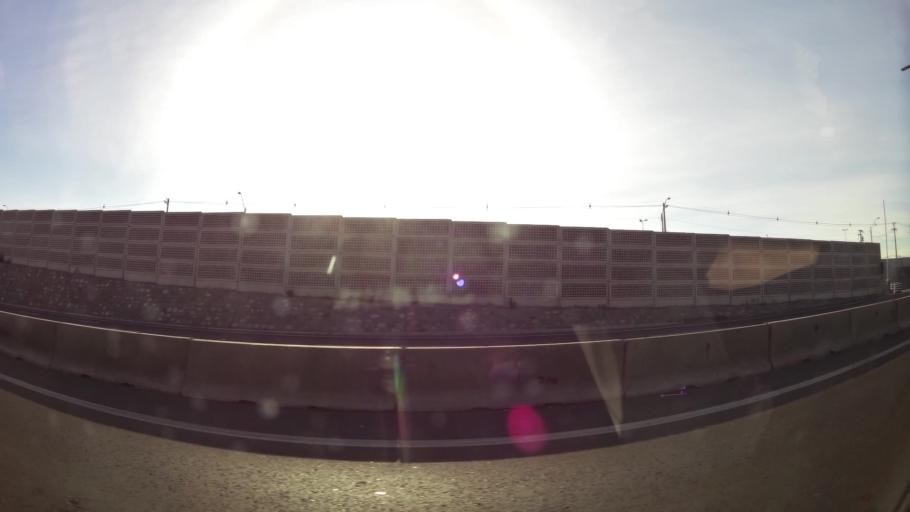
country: CL
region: Santiago Metropolitan
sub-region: Provincia de Santiago
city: La Pintana
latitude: -33.5665
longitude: -70.6133
